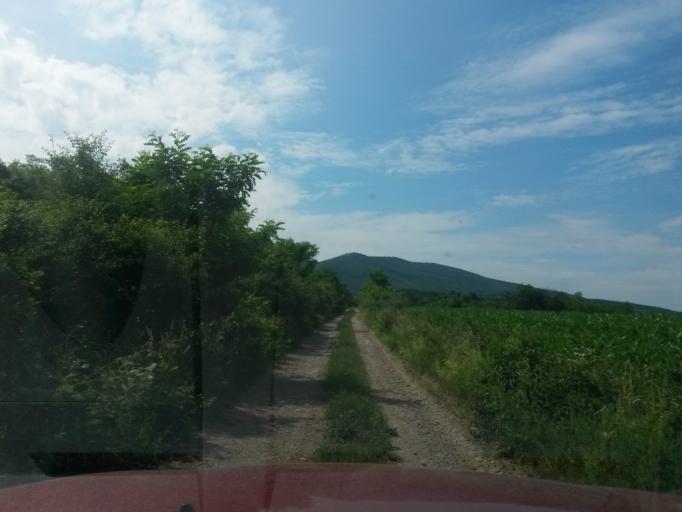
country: SK
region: Kosicky
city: Secovce
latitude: 48.6259
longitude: 21.5018
